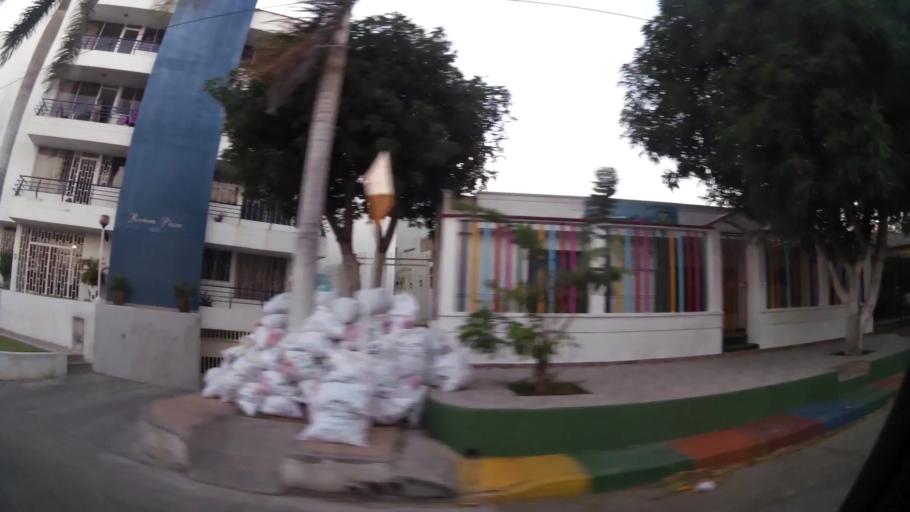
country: CO
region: Atlantico
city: Barranquilla
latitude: 10.9809
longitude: -74.8074
